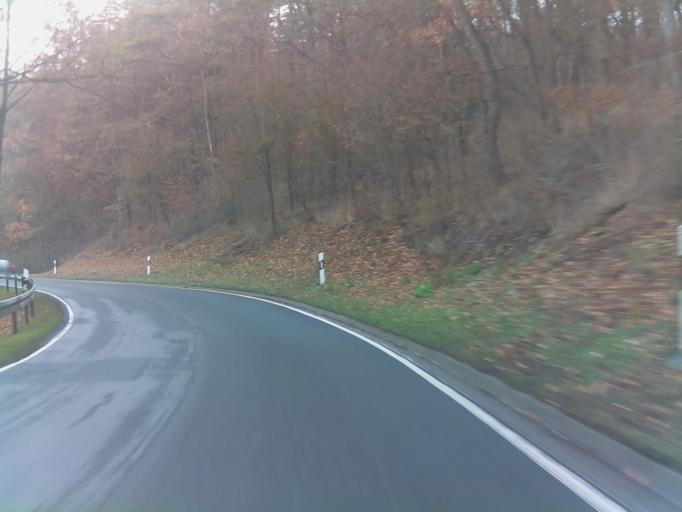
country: DE
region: Thuringia
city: Leutersdorf
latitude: 50.4750
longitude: 10.5548
